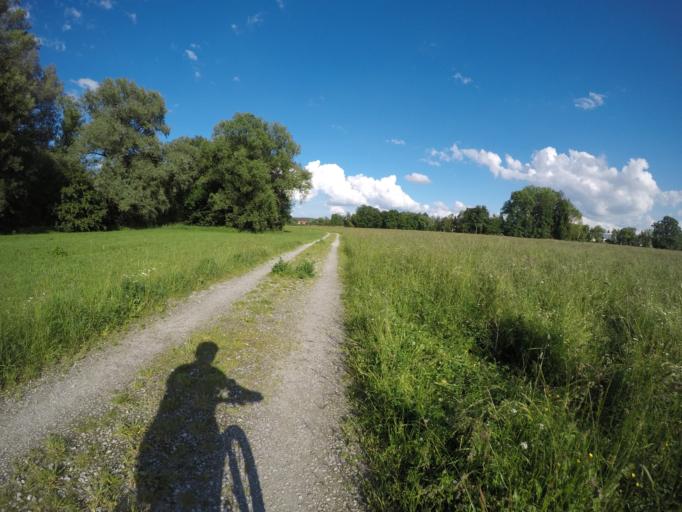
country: DE
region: Bavaria
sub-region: Lower Bavaria
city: Frontenhausen
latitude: 48.5529
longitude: 12.5384
